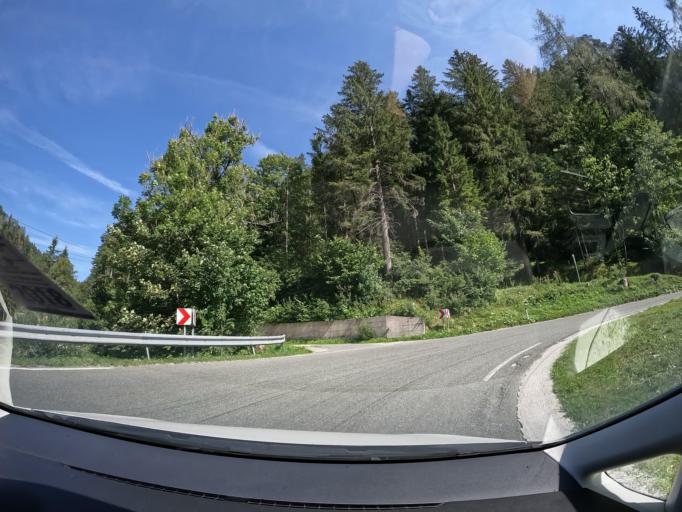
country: AT
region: Carinthia
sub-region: Politischer Bezirk Klagenfurt Land
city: Ludmannsdorf
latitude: 46.5078
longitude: 14.1004
